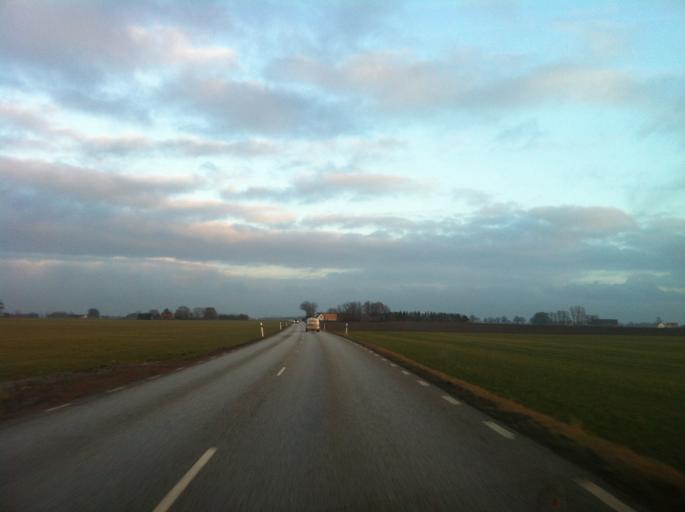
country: SE
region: Skane
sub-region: Kavlinge Kommun
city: Kaevlinge
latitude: 55.8084
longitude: 13.0656
